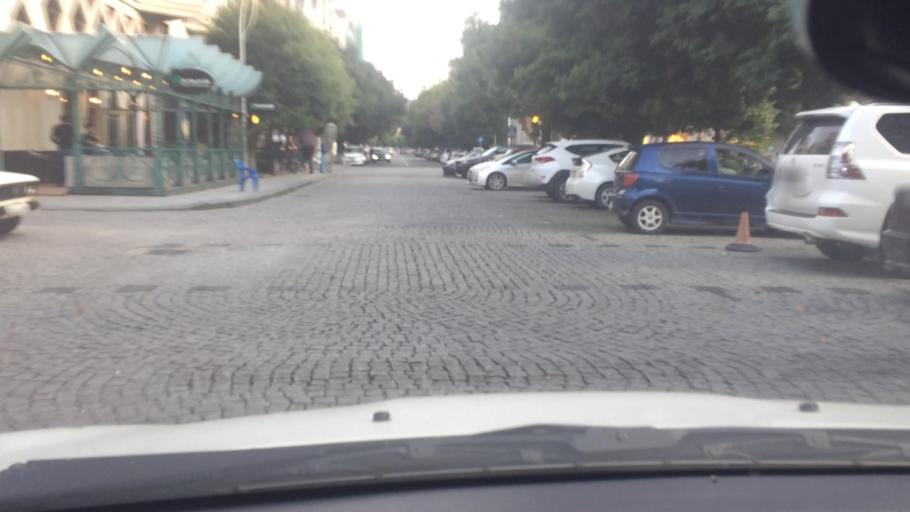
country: GE
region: Ajaria
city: Batumi
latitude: 41.6521
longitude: 41.6334
